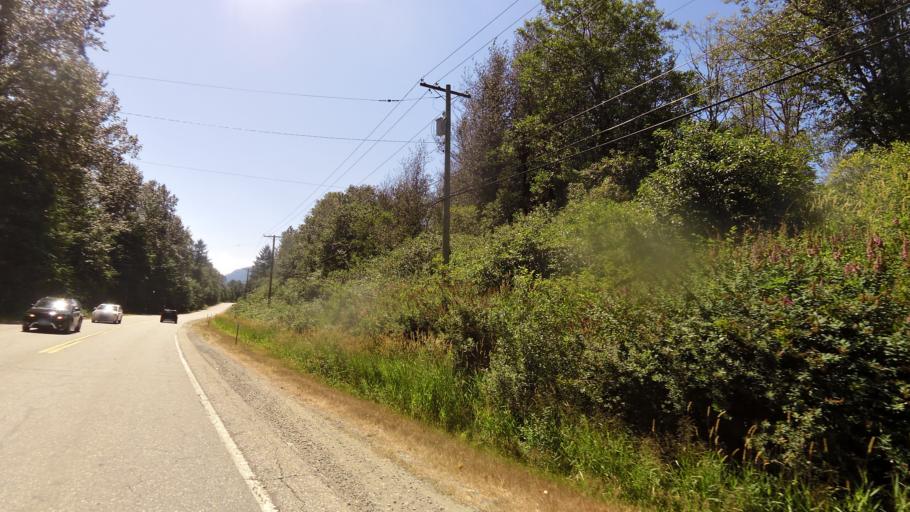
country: CA
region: British Columbia
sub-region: Fraser Valley Regional District
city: Chilliwack
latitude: 49.2105
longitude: -122.0181
